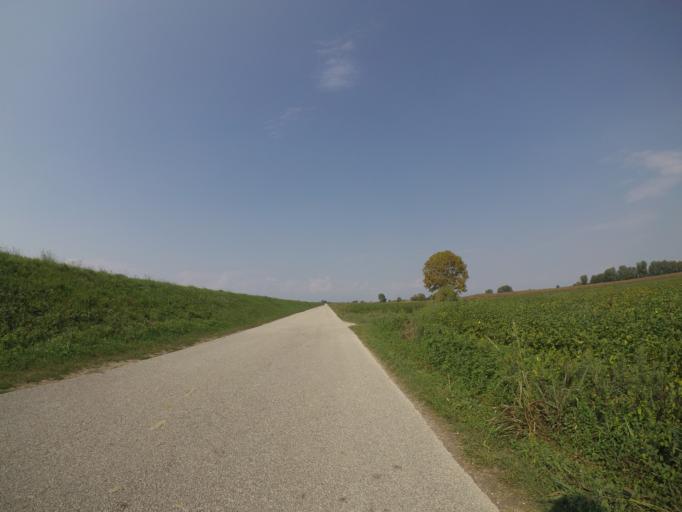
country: IT
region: Friuli Venezia Giulia
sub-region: Provincia di Udine
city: Camino al Tagliamento
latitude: 45.9304
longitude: 12.9223
